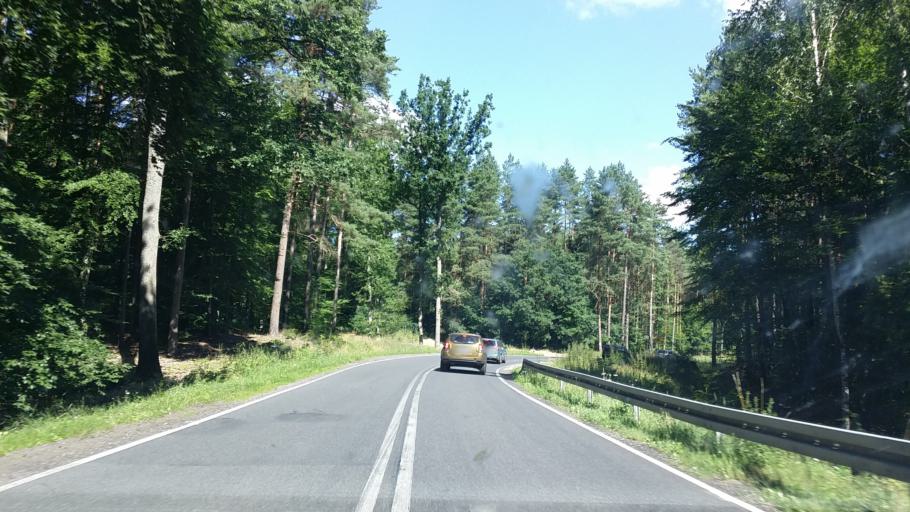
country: PL
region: West Pomeranian Voivodeship
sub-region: Powiat drawski
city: Kalisz Pomorski
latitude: 53.4005
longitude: 15.8439
